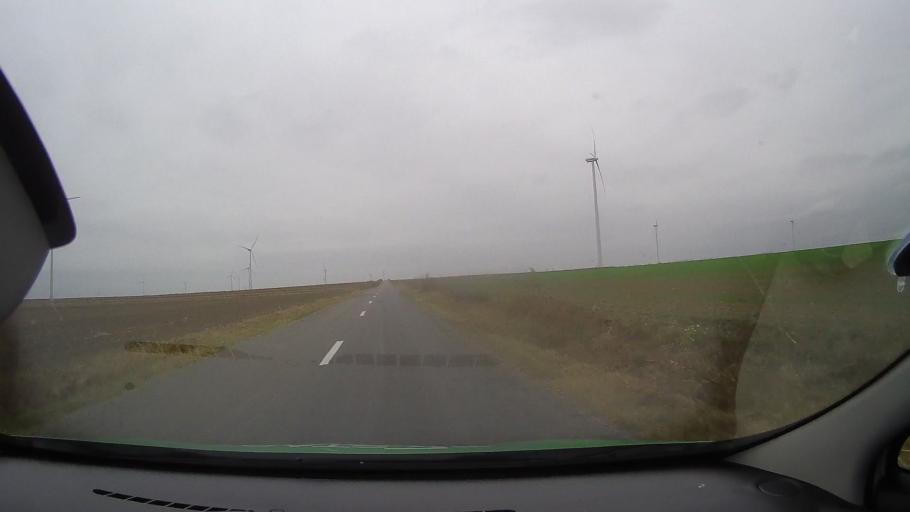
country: RO
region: Constanta
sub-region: Comuna Pantelimon
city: Pantelimon
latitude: 44.5049
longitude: 28.3478
